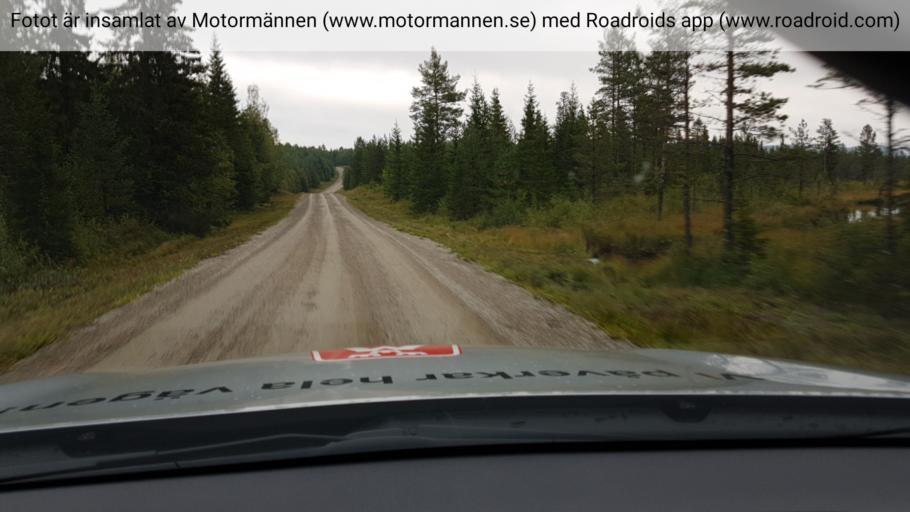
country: SE
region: Jaemtland
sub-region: Braecke Kommun
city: Braecke
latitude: 62.7339
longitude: 15.4763
